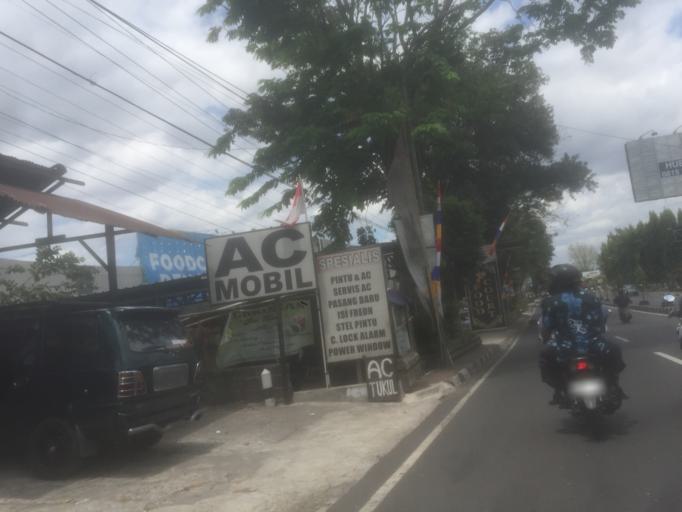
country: ID
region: Daerah Istimewa Yogyakarta
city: Sleman
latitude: -7.7233
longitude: 110.3618
